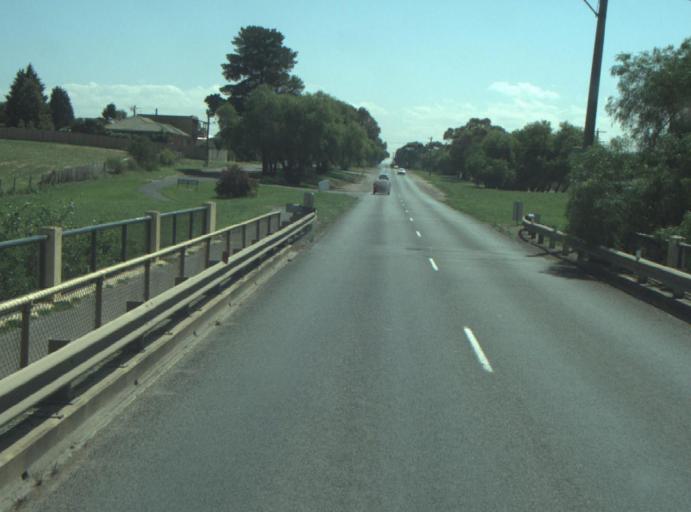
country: AU
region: Victoria
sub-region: Greater Geelong
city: Lara
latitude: -38.0236
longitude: 144.4036
